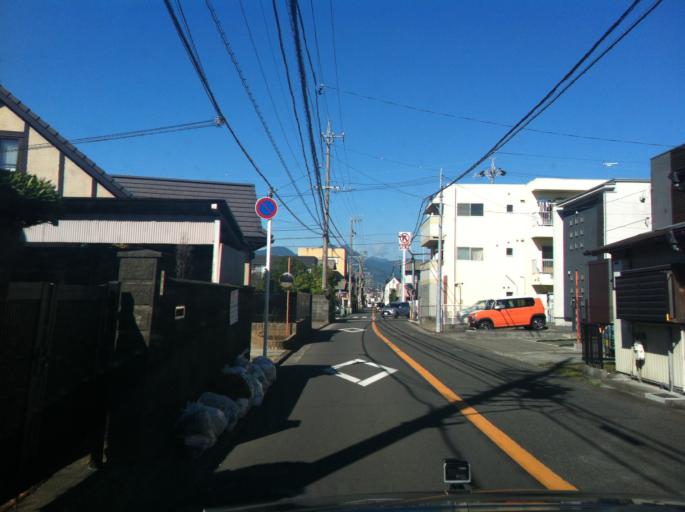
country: JP
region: Shizuoka
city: Shizuoka-shi
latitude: 34.9765
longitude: 138.4262
